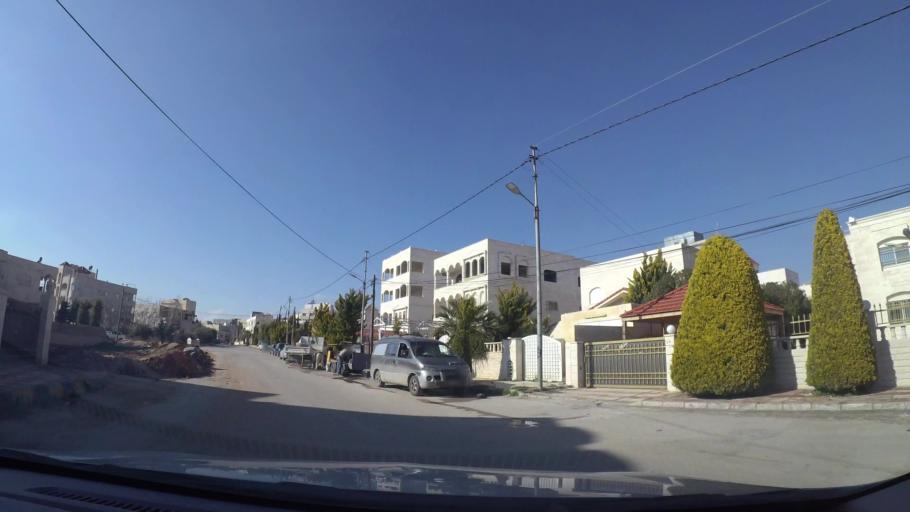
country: JO
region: Amman
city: Al Bunayyat ash Shamaliyah
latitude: 31.9019
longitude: 35.9191
